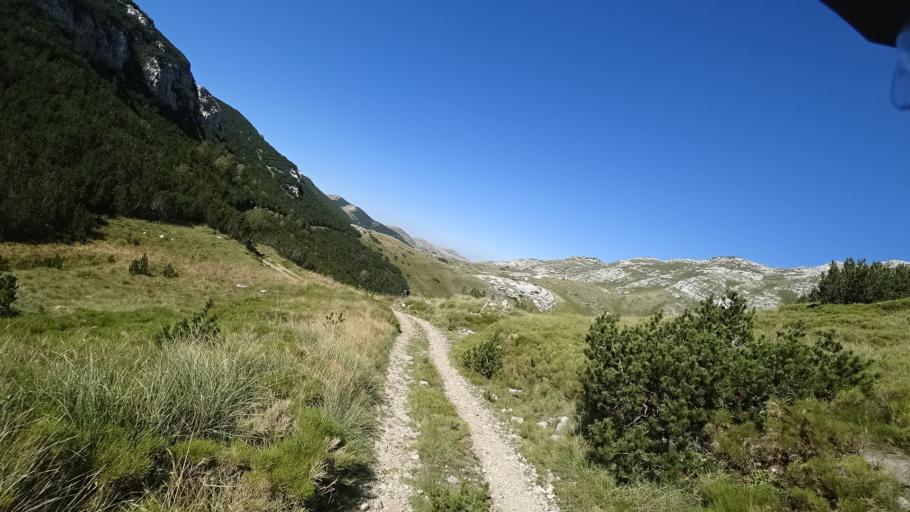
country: HR
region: Splitsko-Dalmatinska
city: Hrvace
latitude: 43.9352
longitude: 16.5979
